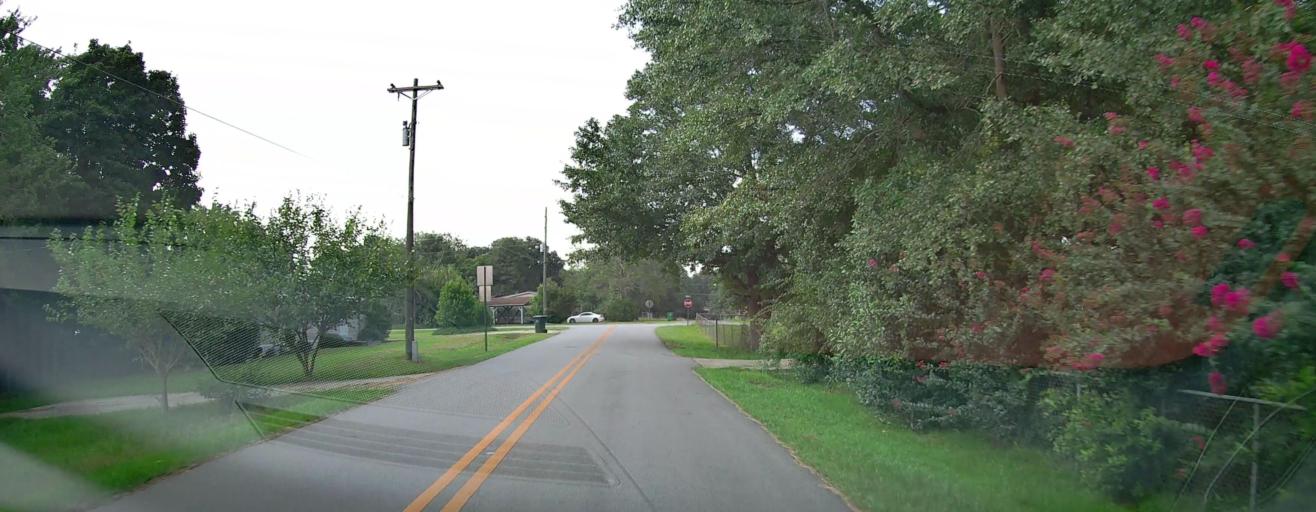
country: US
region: Georgia
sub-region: Houston County
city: Centerville
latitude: 32.6425
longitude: -83.6837
